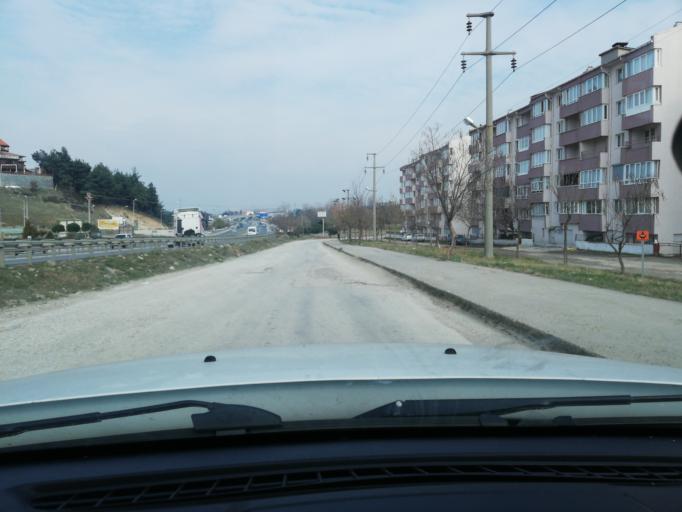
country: TR
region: Edirne
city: Kesan
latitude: 40.8694
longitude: 26.6296
